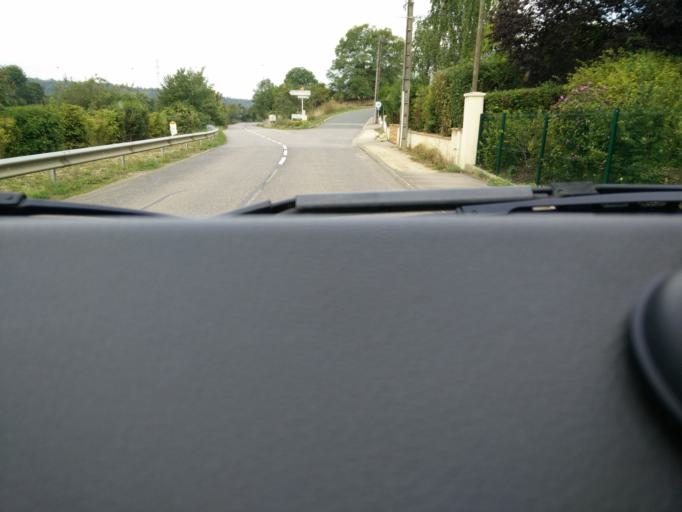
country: FR
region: Lorraine
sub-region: Departement de Meurthe-et-Moselle
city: Belleville
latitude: 48.8209
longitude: 6.1206
